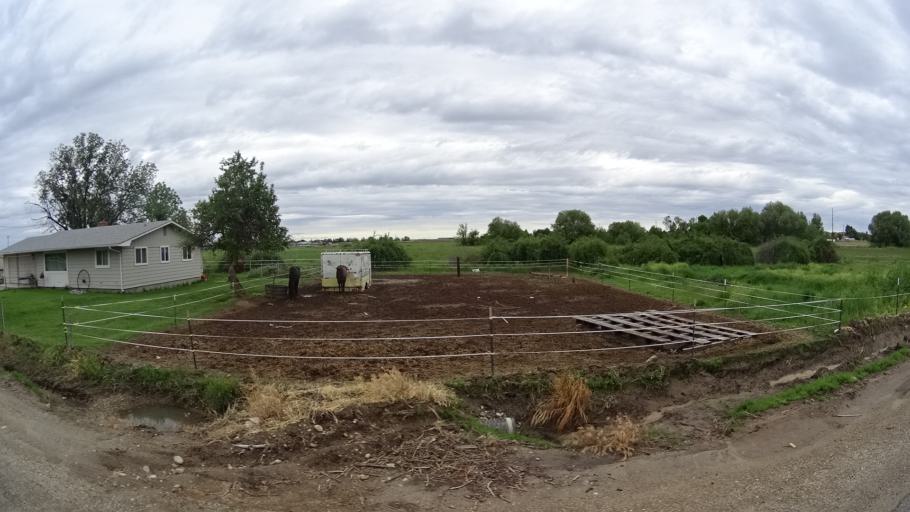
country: US
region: Idaho
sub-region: Ada County
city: Eagle
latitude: 43.7189
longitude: -116.4135
